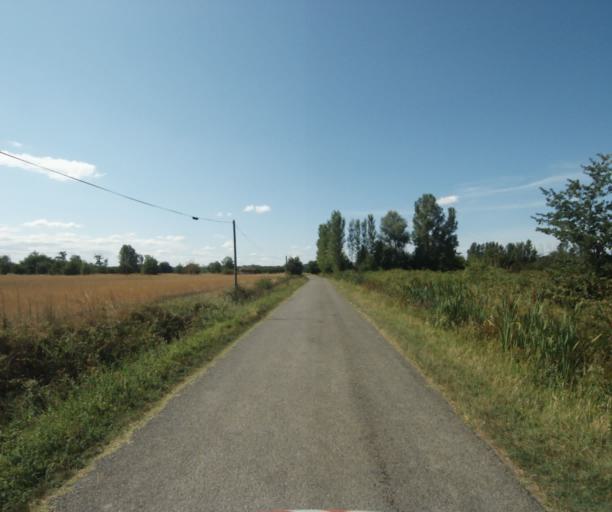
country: FR
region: Midi-Pyrenees
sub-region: Departement de la Haute-Garonne
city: Revel
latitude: 43.4746
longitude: 1.9811
